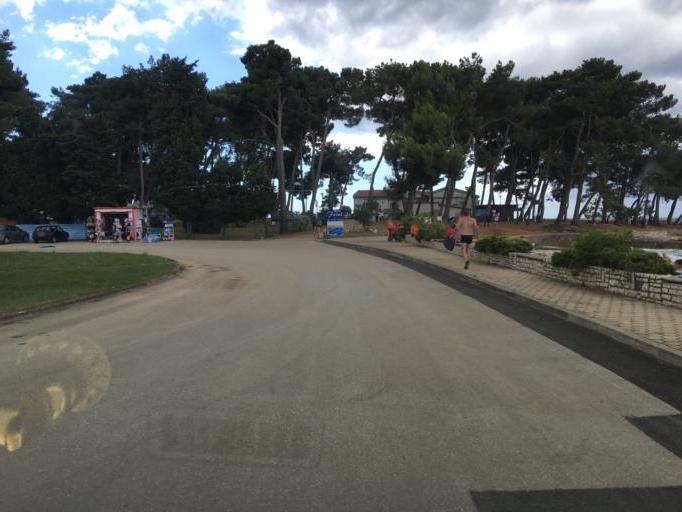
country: HR
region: Istarska
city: Umag
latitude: 45.4875
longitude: 13.4915
